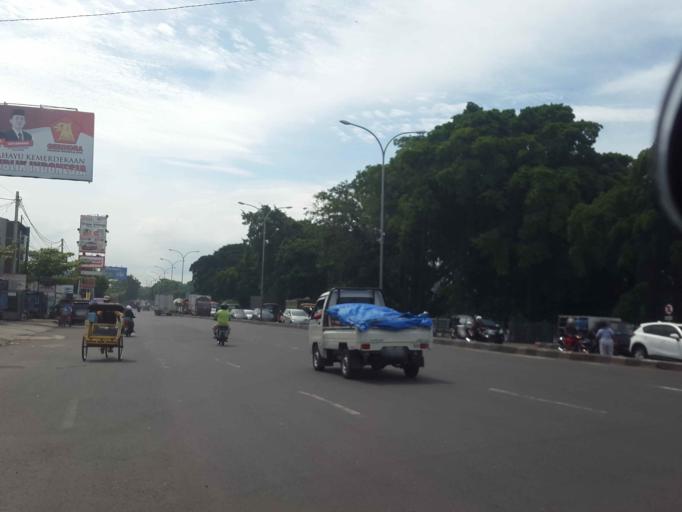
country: ID
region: Central Java
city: Semarang
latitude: -6.9855
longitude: 110.3804
